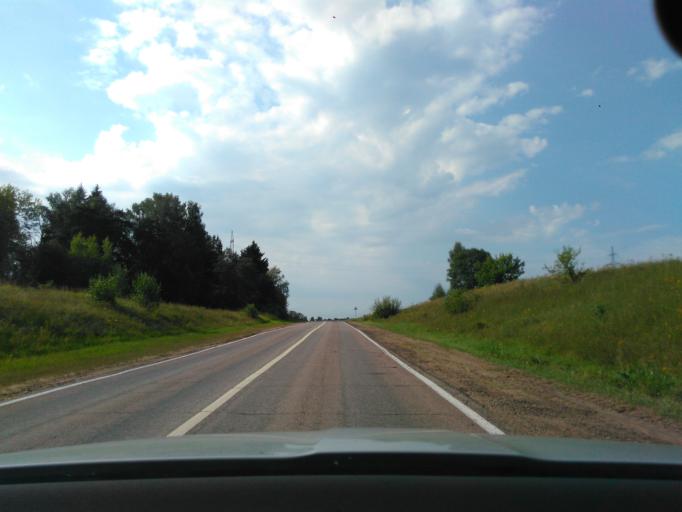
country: RU
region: Moskovskaya
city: Klin
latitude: 56.1493
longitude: 36.7737
